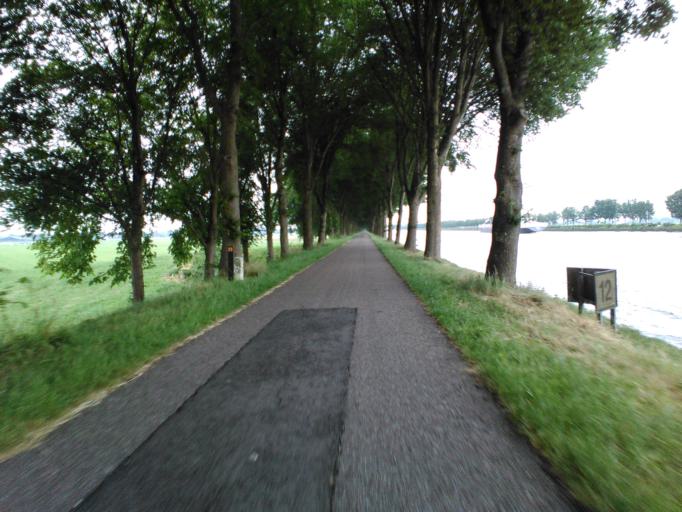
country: NL
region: North Holland
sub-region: Gemeente Amsterdam
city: Driemond
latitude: 52.2849
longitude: 5.0210
